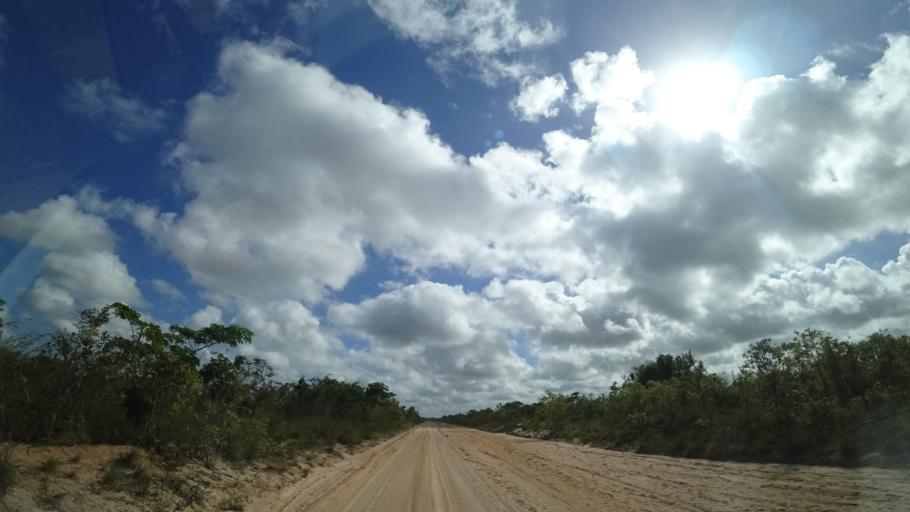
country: MZ
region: Sofala
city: Dondo
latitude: -19.4589
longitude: 34.7189
